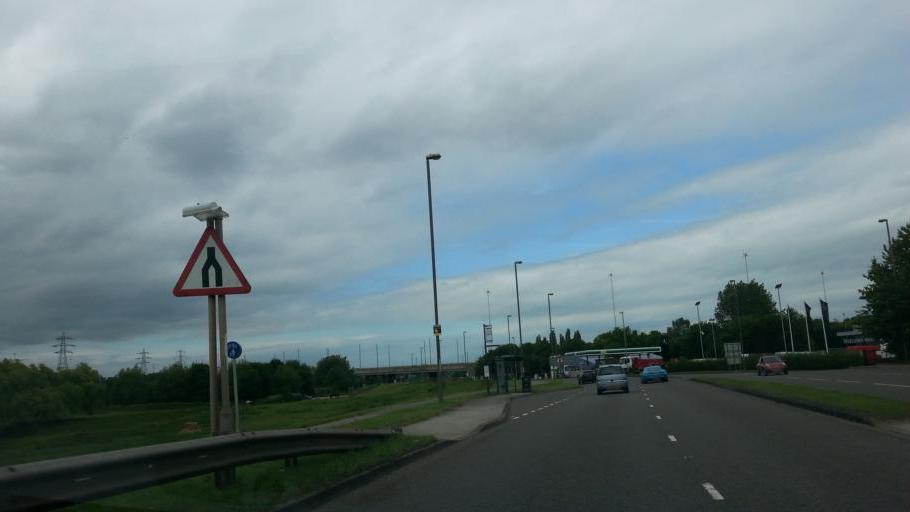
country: GB
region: England
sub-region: Nottinghamshire
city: Ruddington
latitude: 52.9212
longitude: -1.1672
